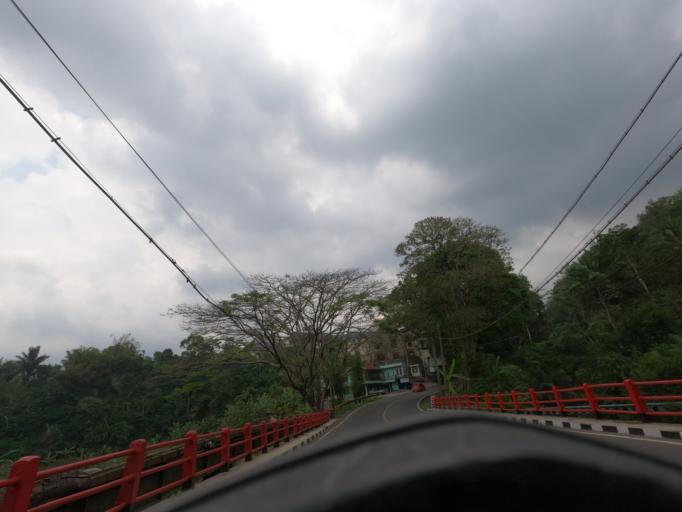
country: ID
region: West Java
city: Ciranjang-hilir
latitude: -6.7939
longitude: 107.0760
